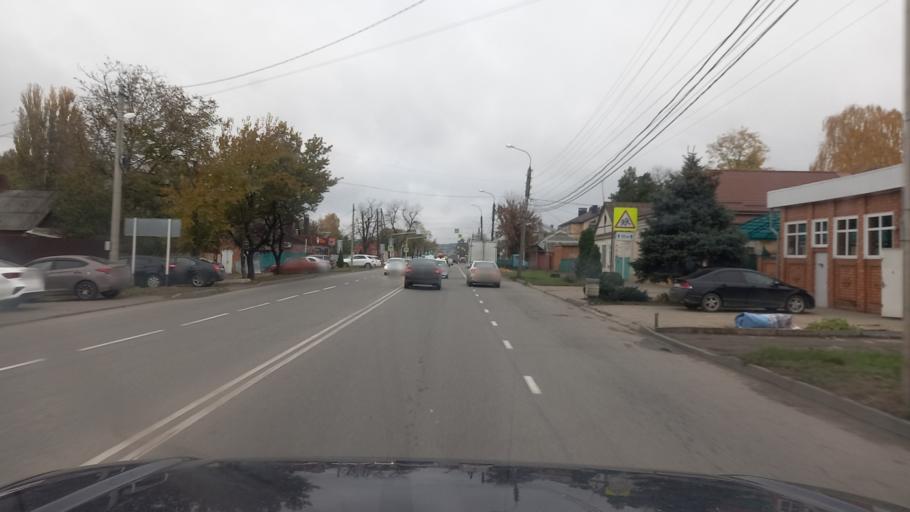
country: RU
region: Adygeya
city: Maykop
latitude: 44.6165
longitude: 40.1167
